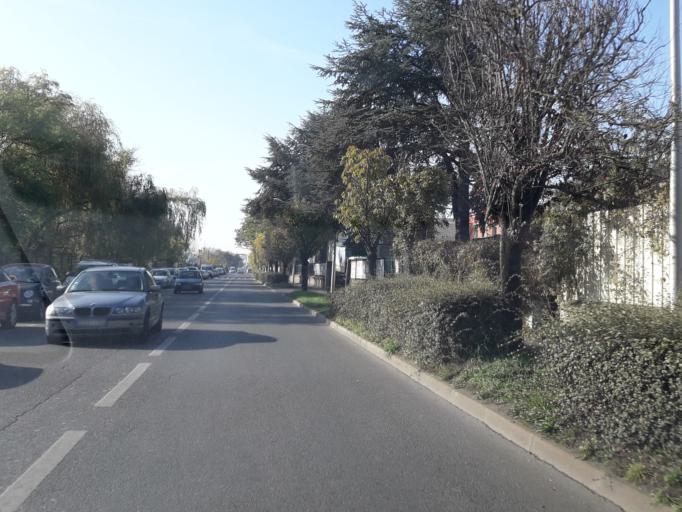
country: FR
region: Ile-de-France
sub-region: Departement de l'Essonne
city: Athis-Mons
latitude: 48.6993
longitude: 2.3964
